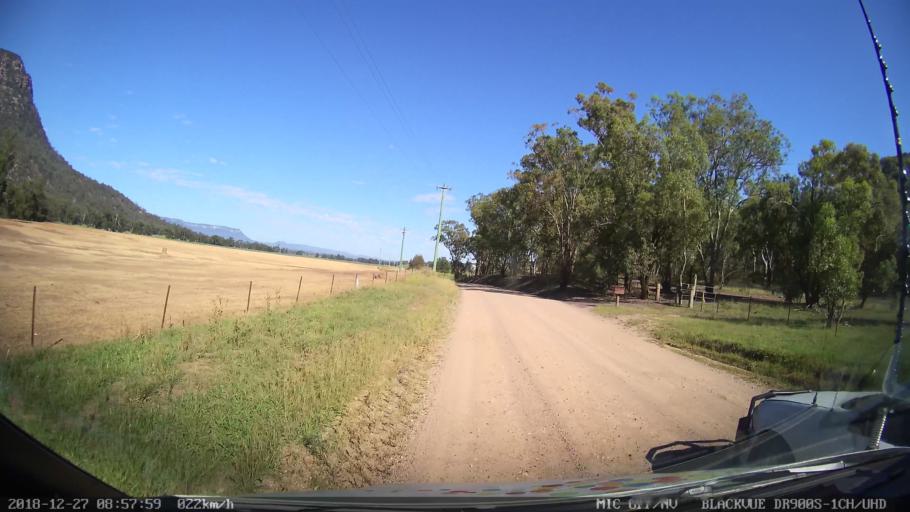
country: AU
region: New South Wales
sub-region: Lithgow
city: Portland
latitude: -33.1077
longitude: 150.2475
